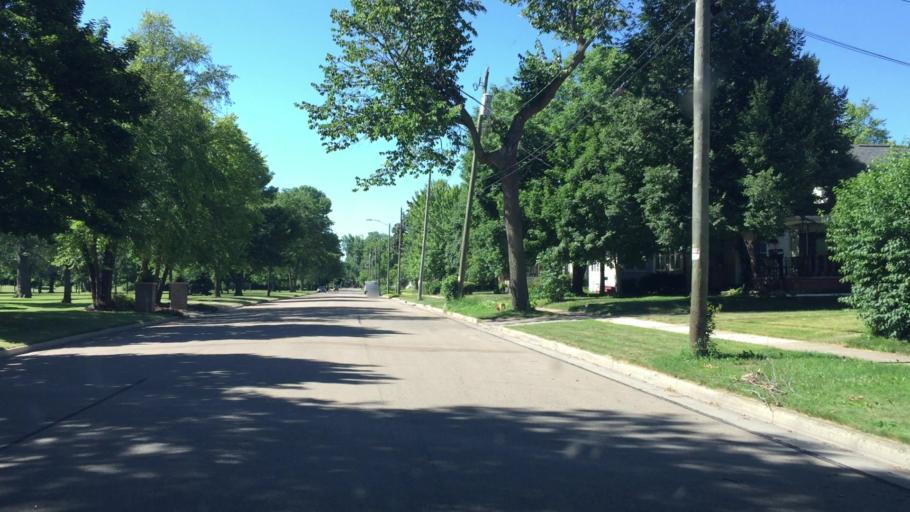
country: US
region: Wisconsin
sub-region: Winnebago County
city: Menasha
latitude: 44.1972
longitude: -88.4420
